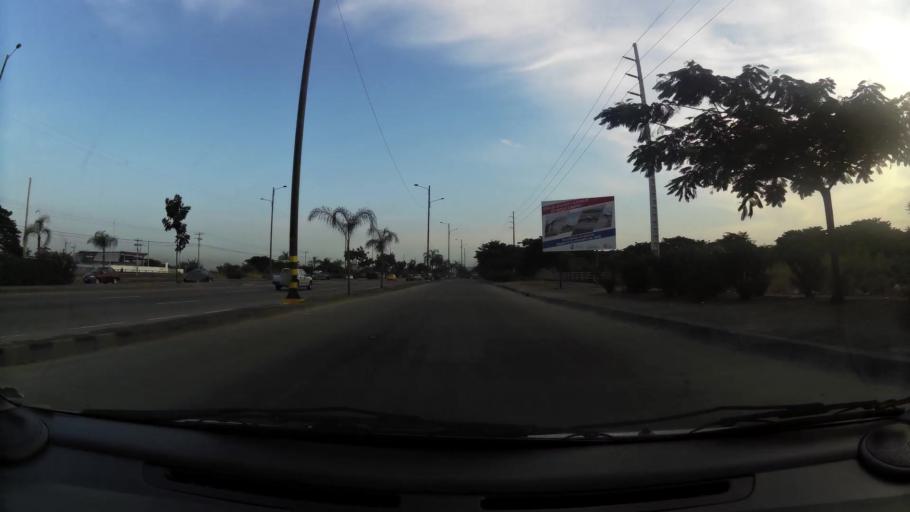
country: EC
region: Guayas
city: Eloy Alfaro
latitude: -2.1158
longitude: -79.8831
